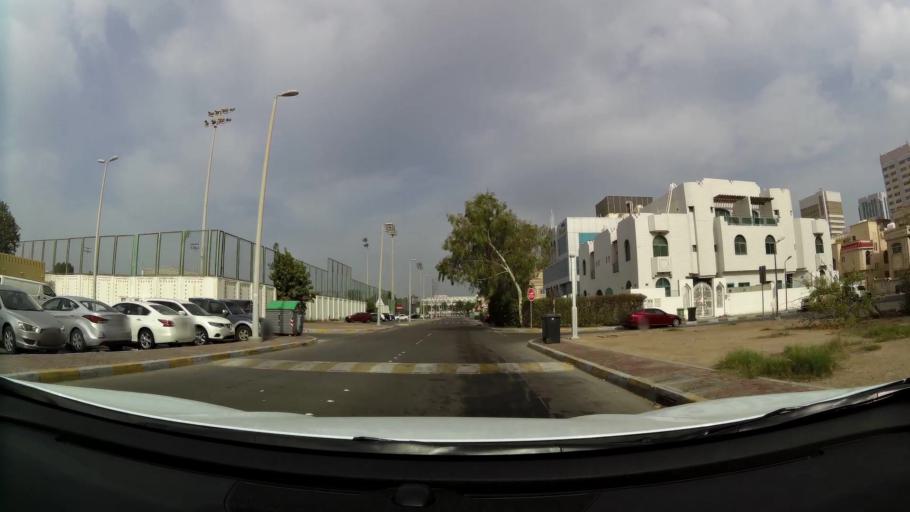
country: AE
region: Abu Dhabi
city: Abu Dhabi
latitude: 24.4596
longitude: 54.3772
